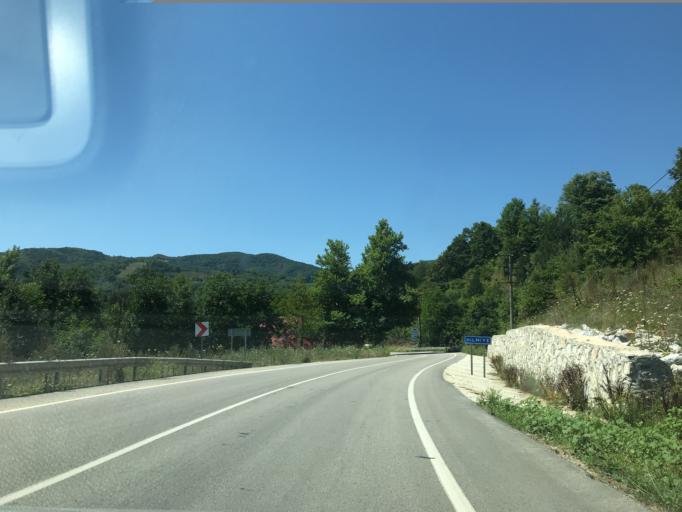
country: TR
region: Bursa
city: Tahtakopru
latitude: 39.9606
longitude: 29.6035
